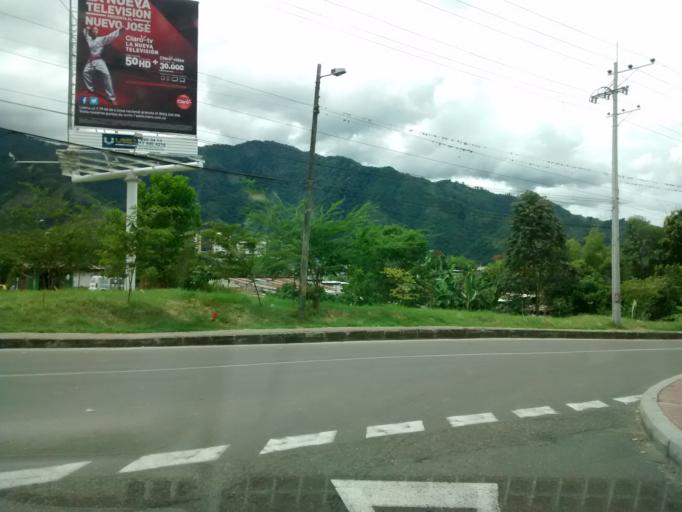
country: CO
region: Tolima
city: Ibague
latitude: 4.4465
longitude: -75.2060
